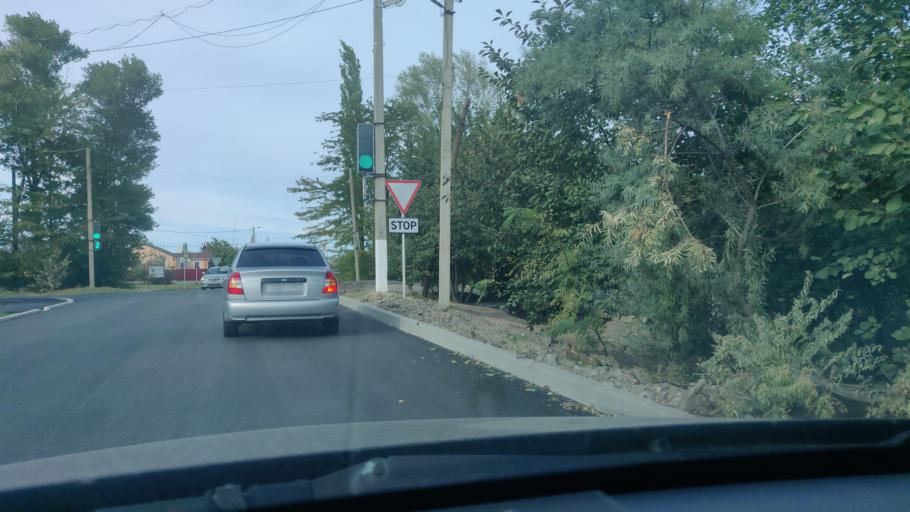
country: RU
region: Rostov
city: Ust'-Donetskiy
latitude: 47.6459
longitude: 40.8730
